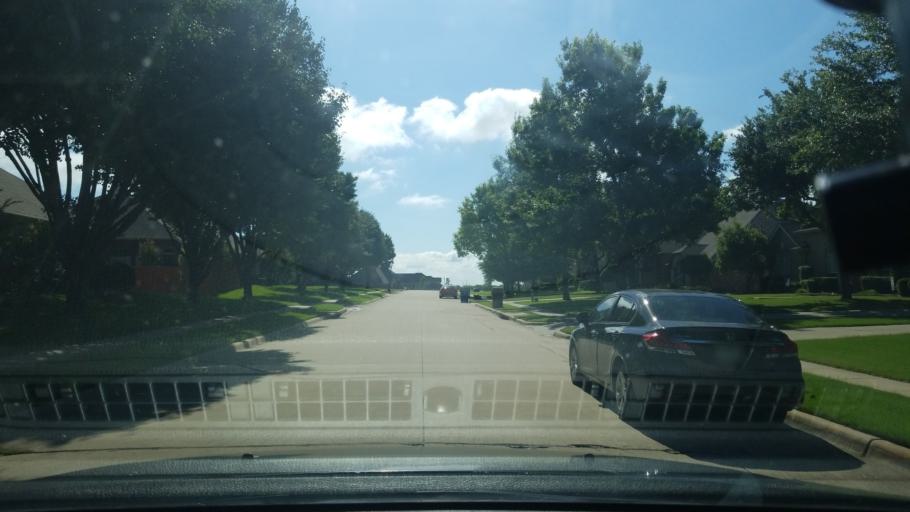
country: US
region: Texas
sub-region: Dallas County
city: Sunnyvale
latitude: 32.8032
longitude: -96.5862
